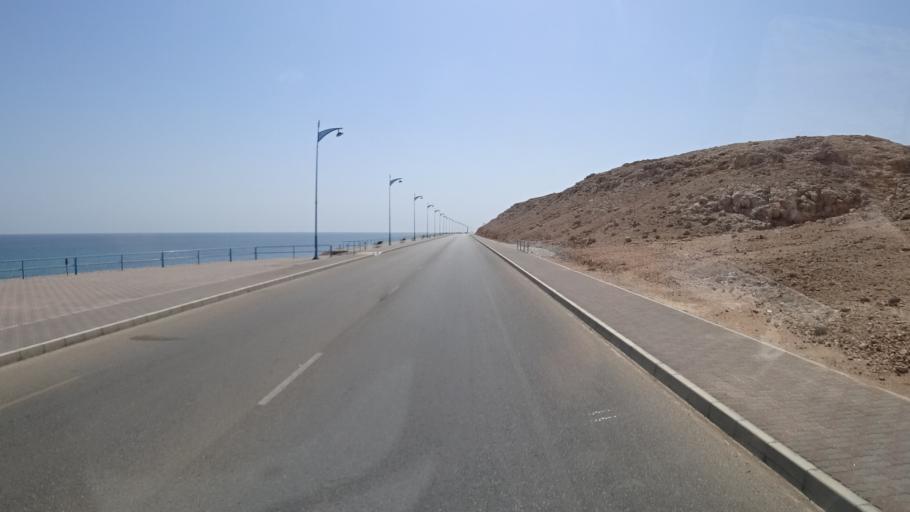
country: OM
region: Ash Sharqiyah
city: Sur
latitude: 22.5663
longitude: 59.5634
